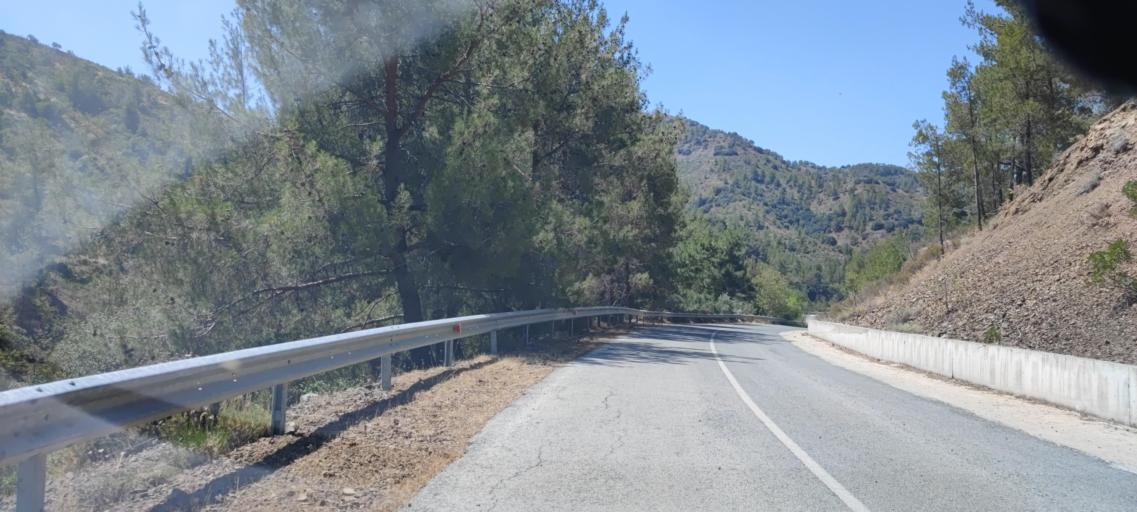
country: CY
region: Lefkosia
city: Kakopetria
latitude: 34.9290
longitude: 32.8038
